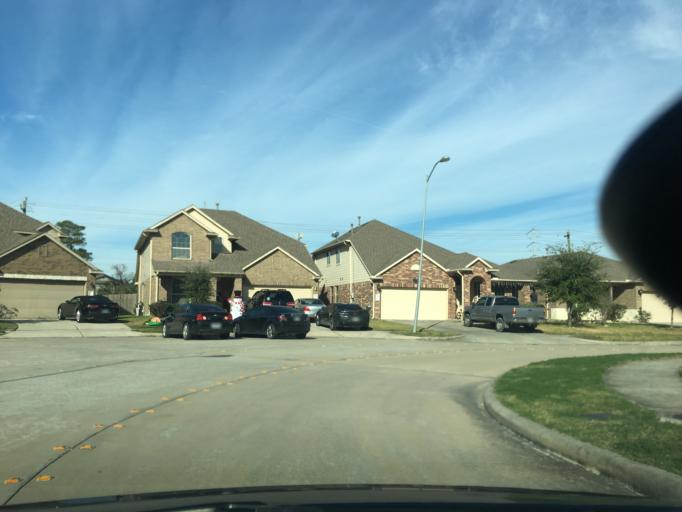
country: US
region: Texas
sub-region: Harris County
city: Cloverleaf
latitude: 29.8154
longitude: -95.1613
